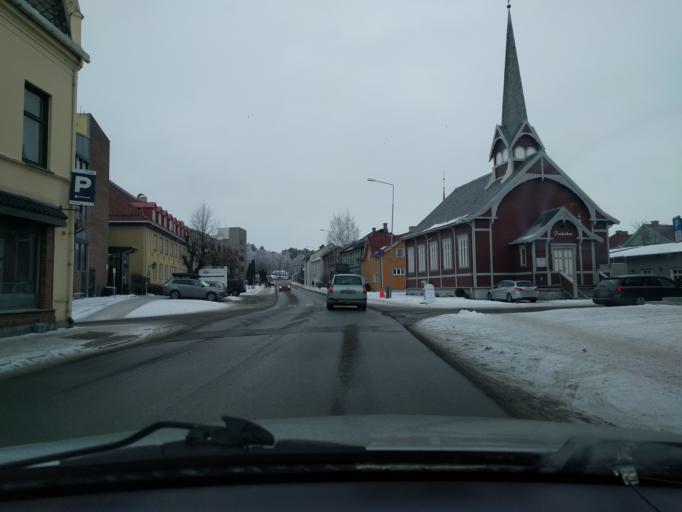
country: NO
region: Hedmark
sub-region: Hamar
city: Hamar
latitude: 60.7969
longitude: 11.0728
